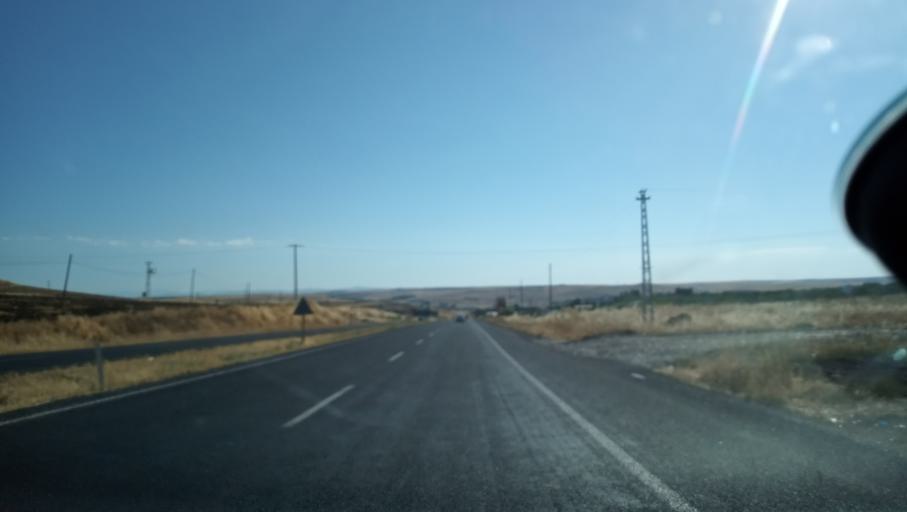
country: TR
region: Diyarbakir
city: Sur
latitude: 37.9858
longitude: 40.3677
